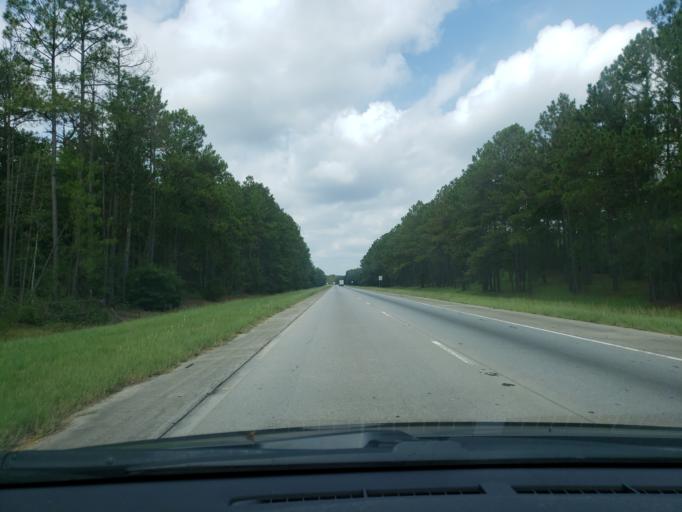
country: US
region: Georgia
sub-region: Treutlen County
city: Soperton
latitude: 32.4220
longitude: -82.4144
